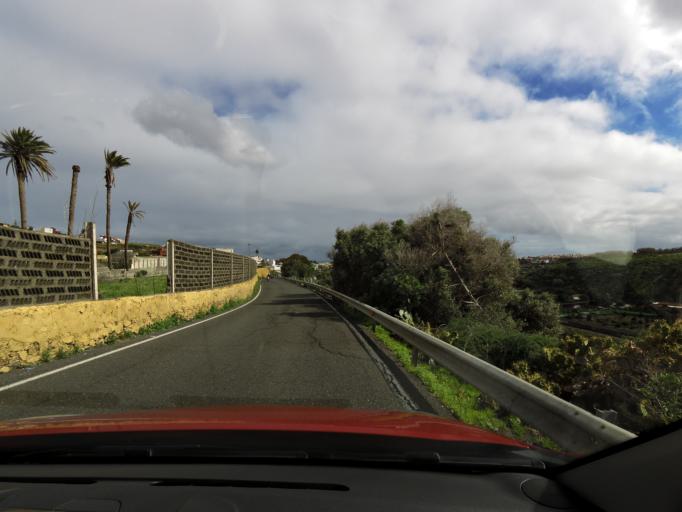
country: ES
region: Canary Islands
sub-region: Provincia de Las Palmas
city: Telde
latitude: 28.0075
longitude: -15.4270
